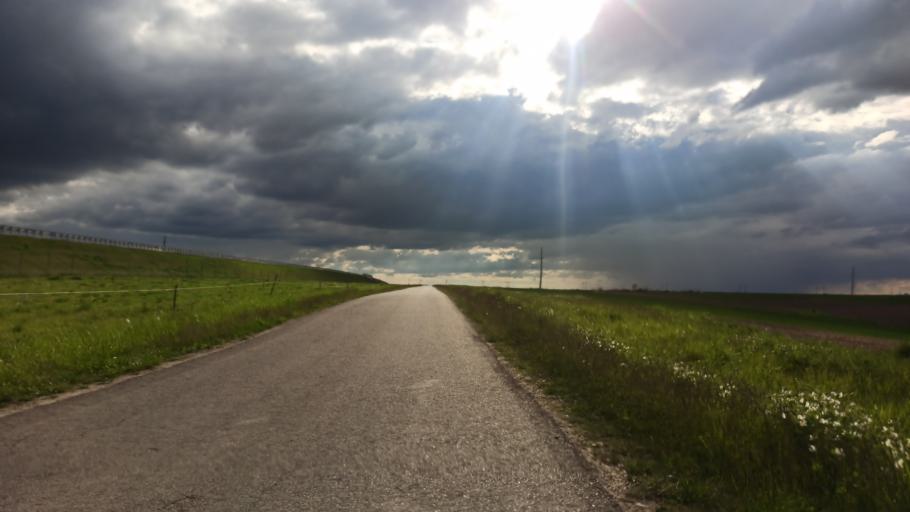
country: PL
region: Subcarpathian Voivodeship
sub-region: Powiat jaroslawski
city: Sosnica
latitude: 49.9154
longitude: 22.8547
